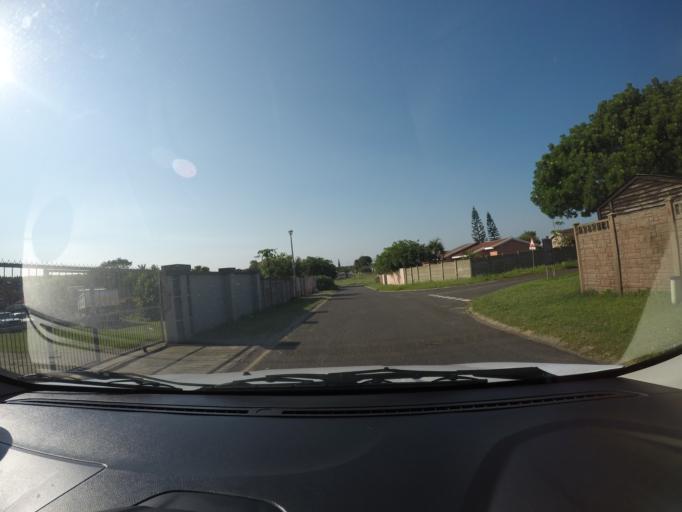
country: ZA
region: KwaZulu-Natal
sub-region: uThungulu District Municipality
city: Richards Bay
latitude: -28.7171
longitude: 32.0332
